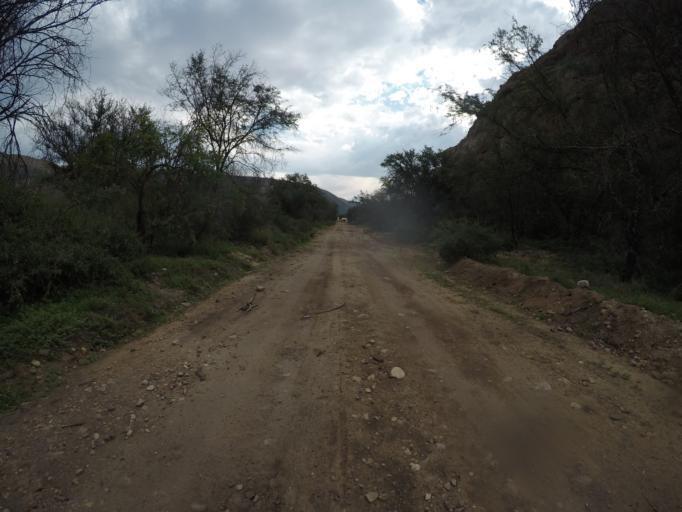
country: ZA
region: Eastern Cape
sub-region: Cacadu District Municipality
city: Kareedouw
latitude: -33.6037
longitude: 24.2024
